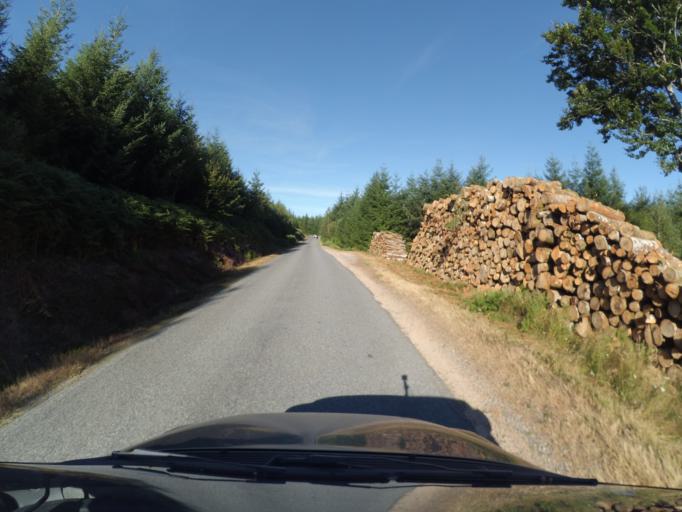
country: FR
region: Limousin
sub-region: Departement de la Creuse
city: Banize
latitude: 45.7812
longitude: 1.9762
